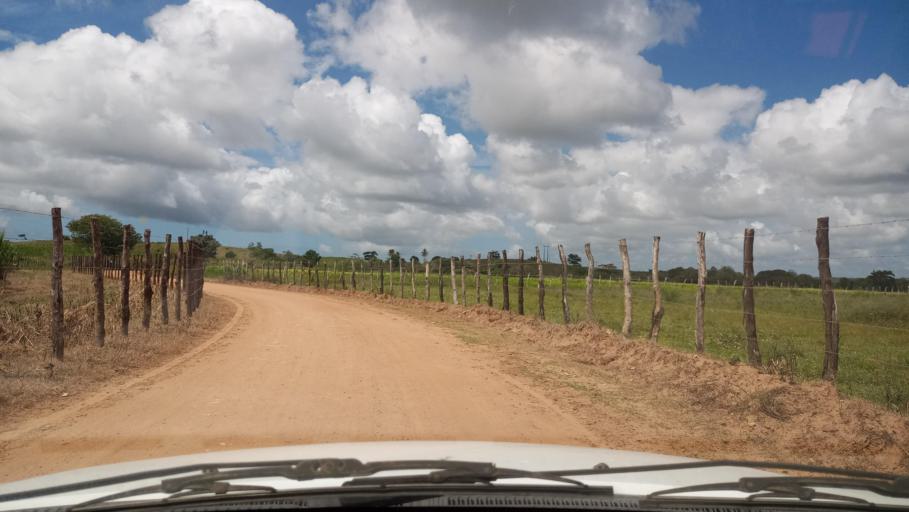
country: BR
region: Rio Grande do Norte
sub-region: Goianinha
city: Goianinha
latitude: -6.2614
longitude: -35.2430
